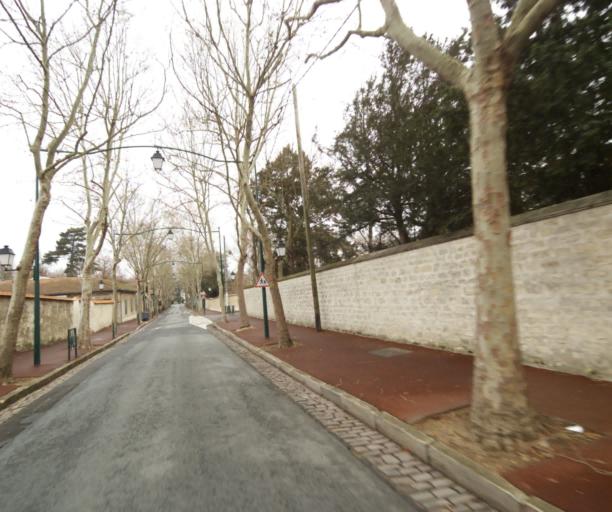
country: FR
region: Ile-de-France
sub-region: Departement des Yvelines
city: Chatou
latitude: 48.8731
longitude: 2.1691
